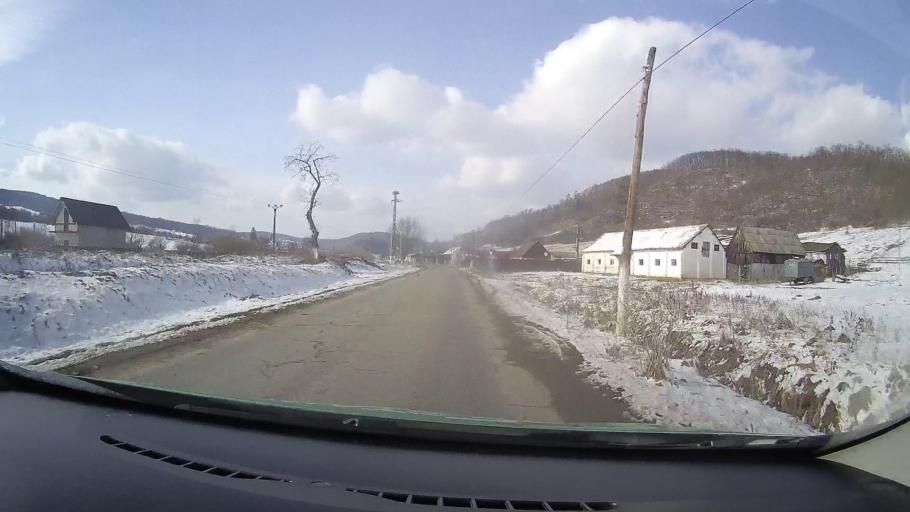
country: RO
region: Sibiu
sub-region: Comuna Iacobeni
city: Iacobeni
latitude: 46.0439
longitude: 24.7275
